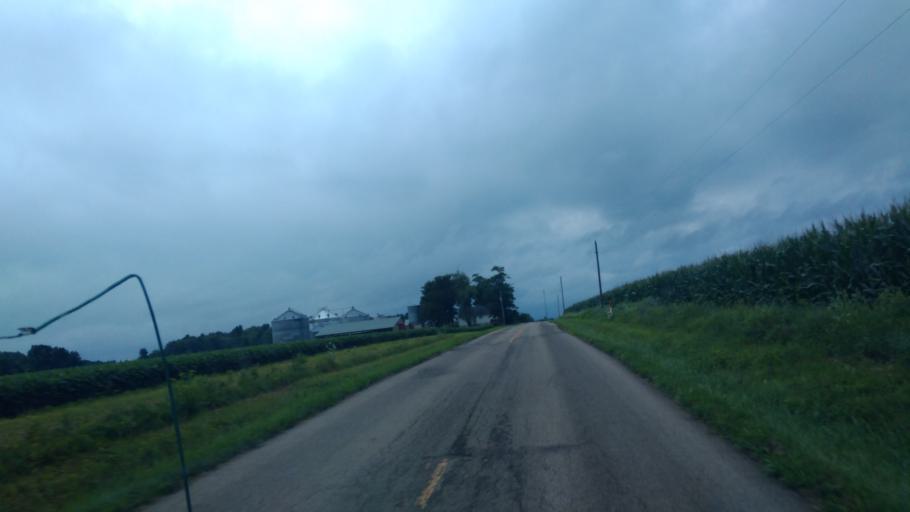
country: US
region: Ohio
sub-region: Knox County
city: Gambier
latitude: 40.2914
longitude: -82.3236
